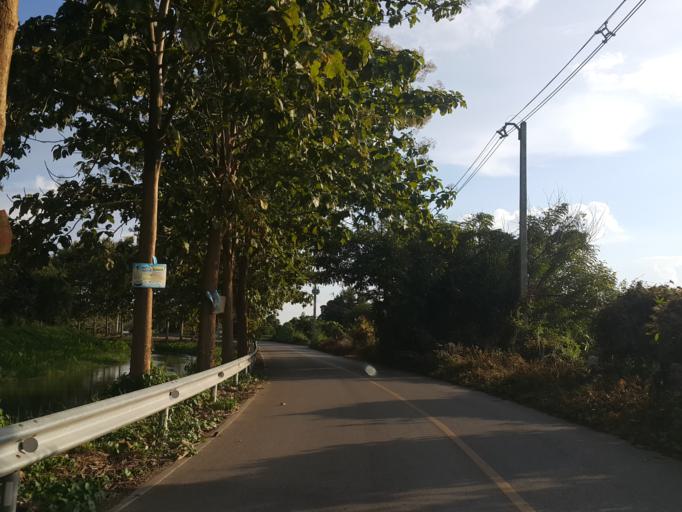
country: TH
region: Chiang Mai
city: Mae Taeng
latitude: 19.0303
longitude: 98.9845
